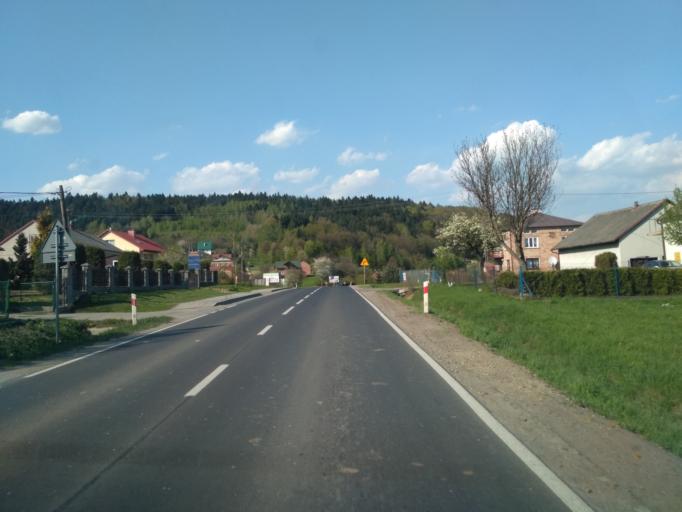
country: PL
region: Subcarpathian Voivodeship
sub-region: Powiat strzyzowski
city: Frysztak
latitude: 49.8483
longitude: 21.6121
